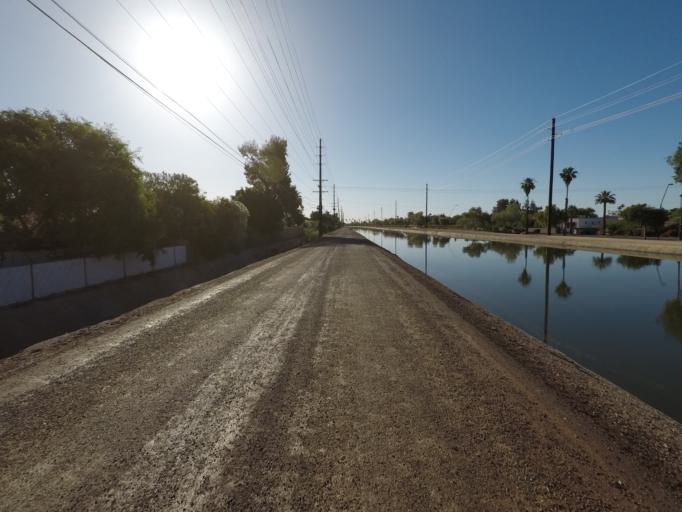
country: US
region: Arizona
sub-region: Maricopa County
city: Paradise Valley
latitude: 33.4917
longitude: -111.9553
